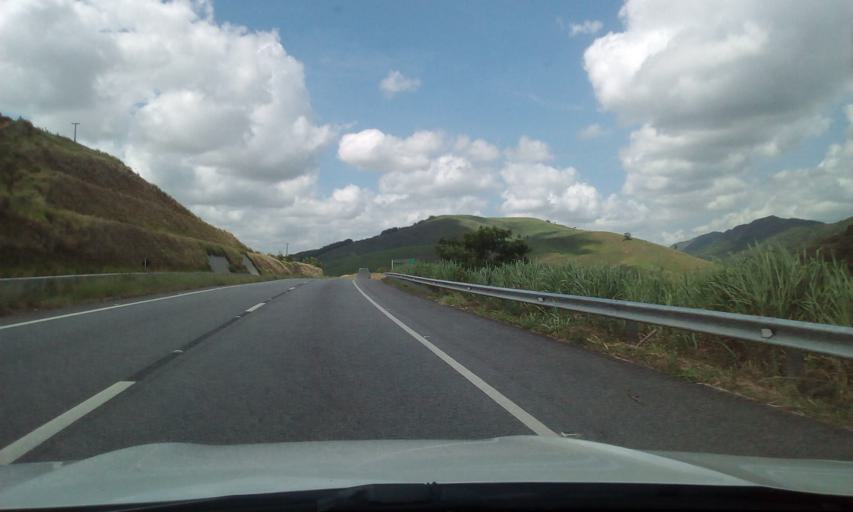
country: BR
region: Alagoas
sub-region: Flexeiras
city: Flexeiras
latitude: -9.2518
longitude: -35.7697
